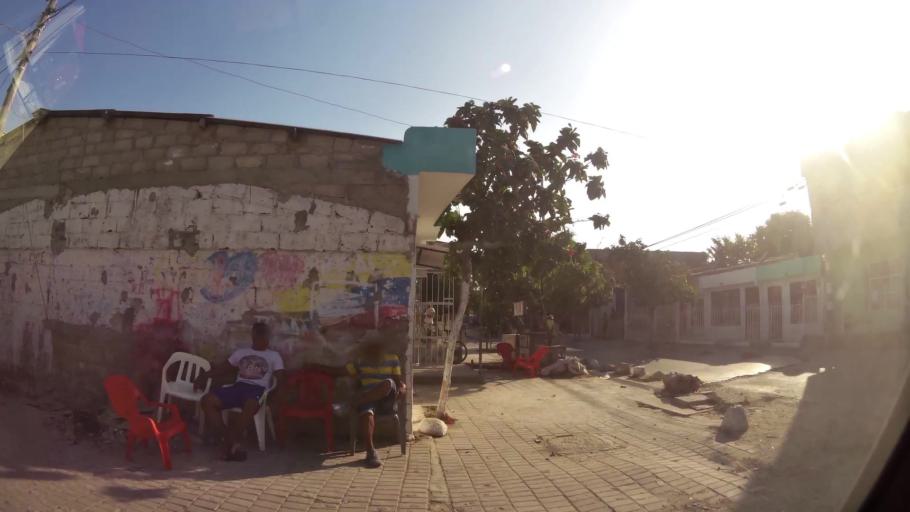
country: CO
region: Bolivar
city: Cartagena
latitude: 10.4108
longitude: -75.4961
